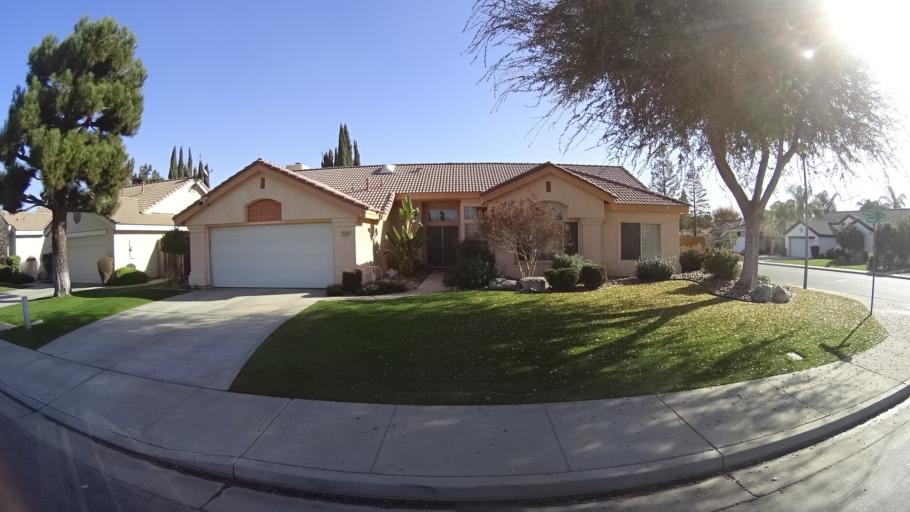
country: US
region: California
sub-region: Kern County
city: Greenfield
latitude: 35.2771
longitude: -119.0428
